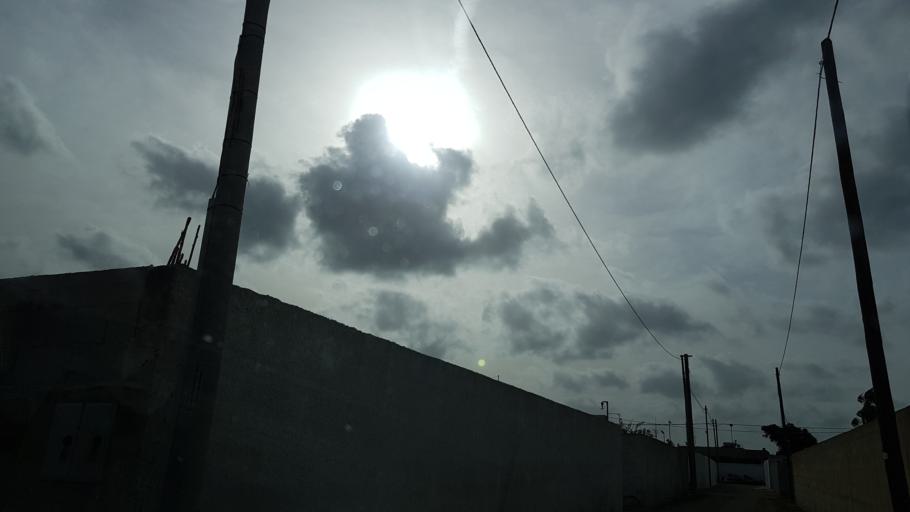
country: IT
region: Apulia
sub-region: Provincia di Brindisi
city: Materdomini
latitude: 40.6745
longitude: 17.9425
